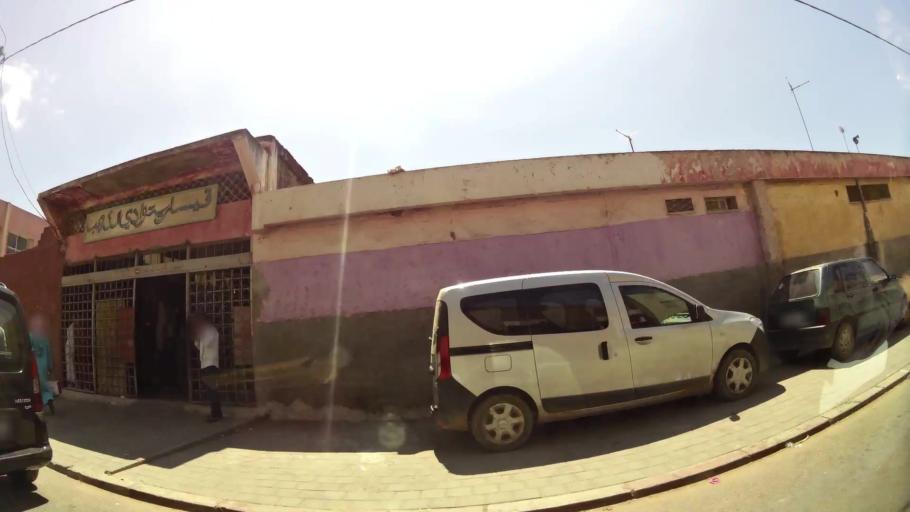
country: MA
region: Gharb-Chrarda-Beni Hssen
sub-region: Kenitra Province
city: Kenitra
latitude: 34.2513
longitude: -6.5502
